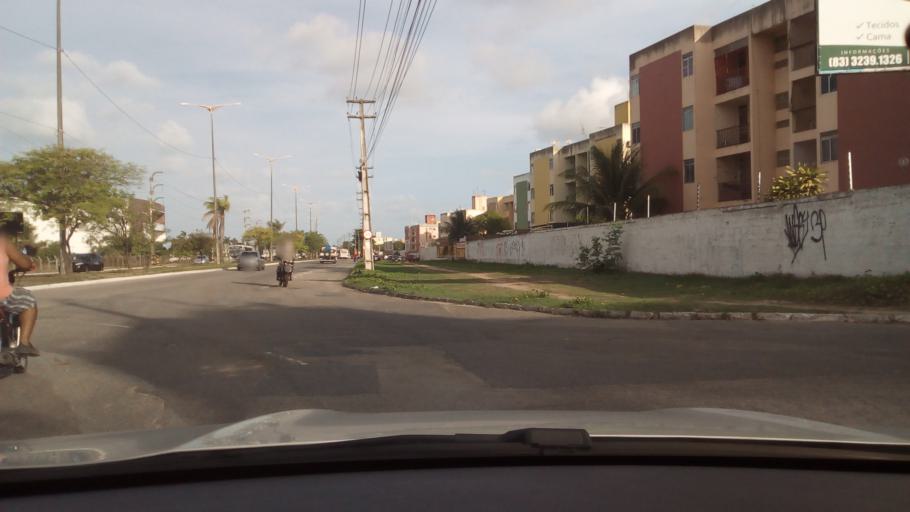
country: BR
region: Paraiba
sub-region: Joao Pessoa
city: Joao Pessoa
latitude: -7.1628
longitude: -34.8341
